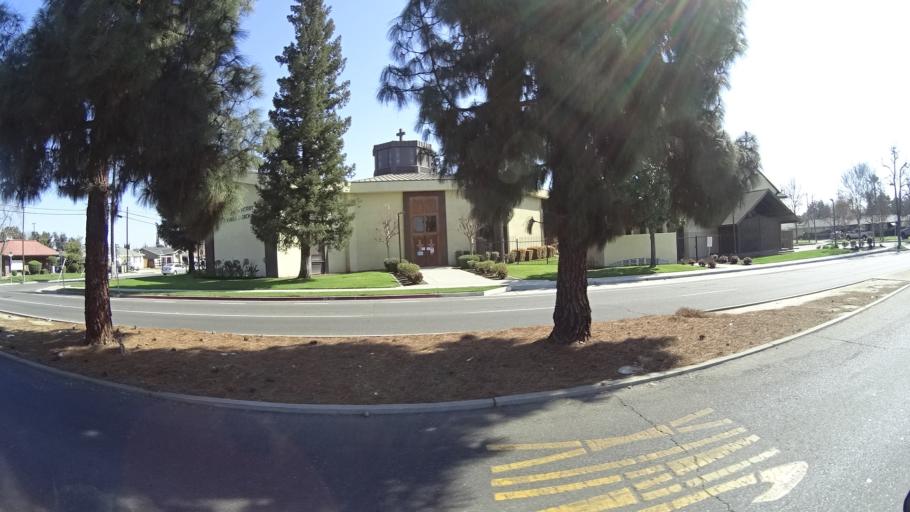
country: US
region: California
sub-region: Fresno County
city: Fresno
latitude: 36.7763
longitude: -119.8267
